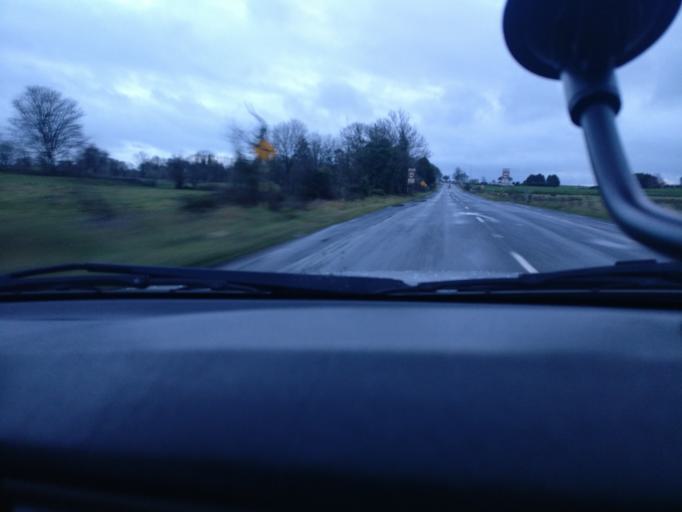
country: IE
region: Connaught
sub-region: County Galway
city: Loughrea
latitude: 53.2360
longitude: -8.4528
